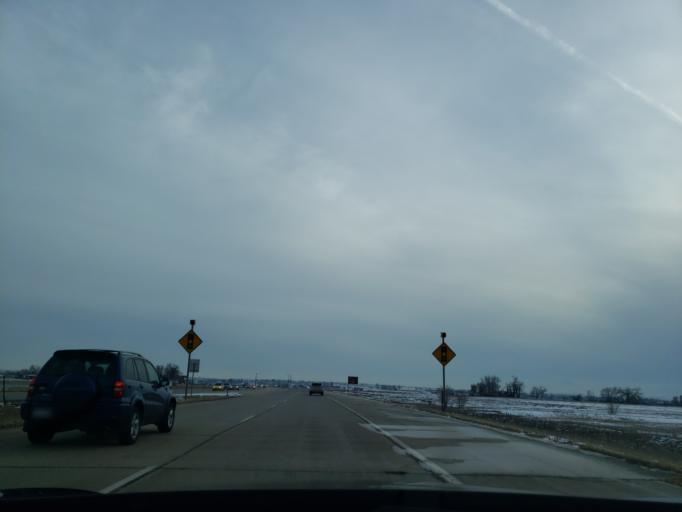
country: US
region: Colorado
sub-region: Larimer County
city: Berthoud
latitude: 40.3099
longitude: -105.1061
